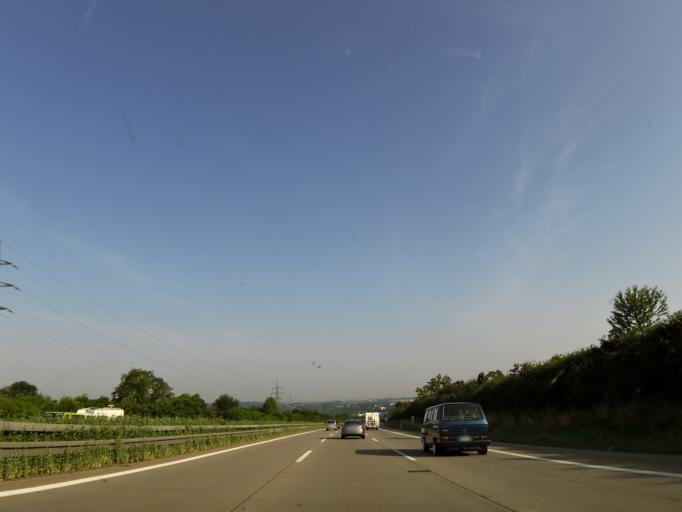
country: DE
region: Baden-Wuerttemberg
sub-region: Regierungsbezirk Stuttgart
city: Wendlingen am Neckar
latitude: 48.6583
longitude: 9.3800
